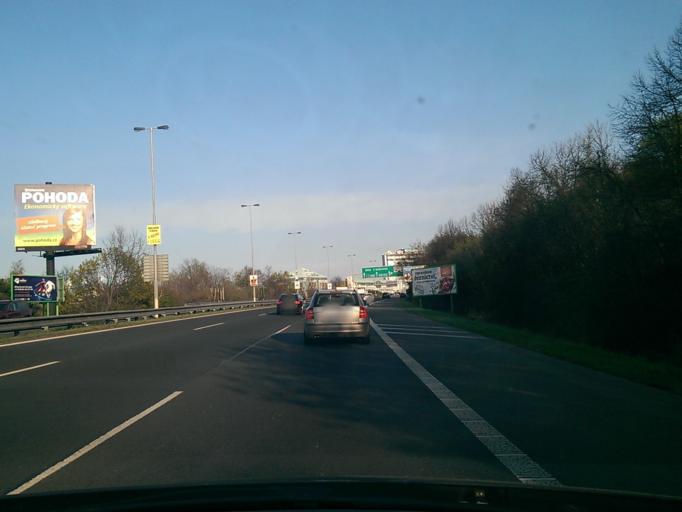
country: CZ
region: Central Bohemia
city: Vestec
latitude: 50.0398
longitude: 14.4852
